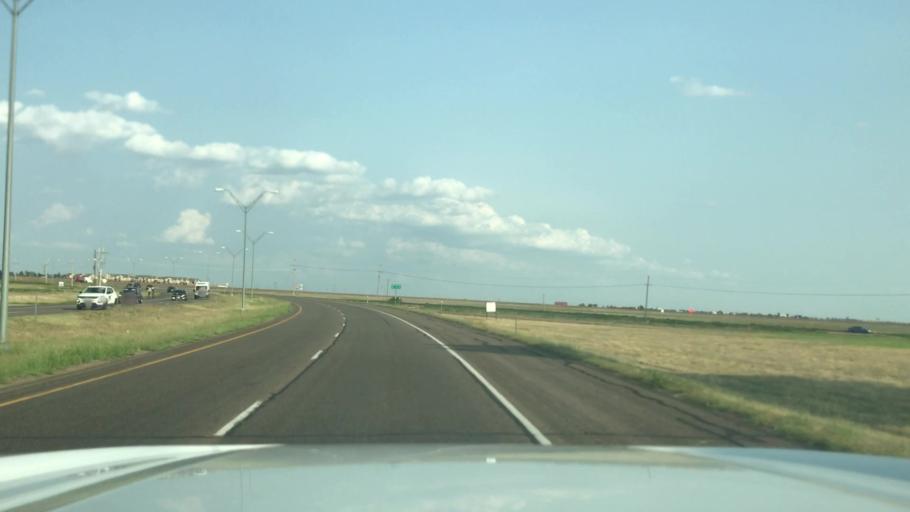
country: US
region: Texas
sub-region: Randall County
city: Canyon
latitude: 35.1188
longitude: -101.9357
